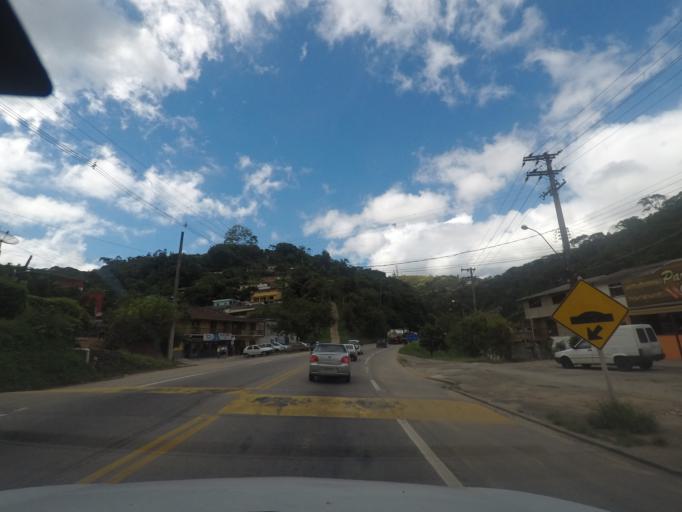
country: BR
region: Rio de Janeiro
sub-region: Teresopolis
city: Teresopolis
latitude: -22.3948
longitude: -42.9529
